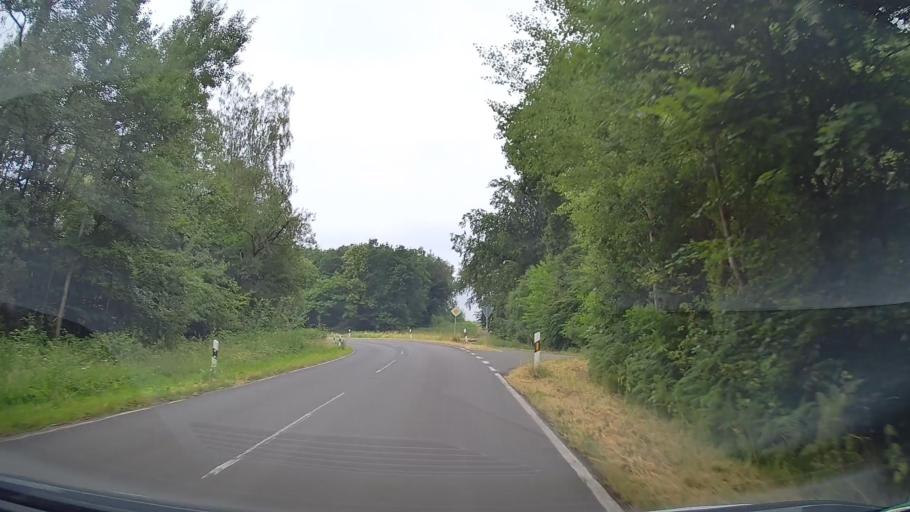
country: DE
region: Lower Saxony
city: Rinteln
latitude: 52.1506
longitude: 9.0562
